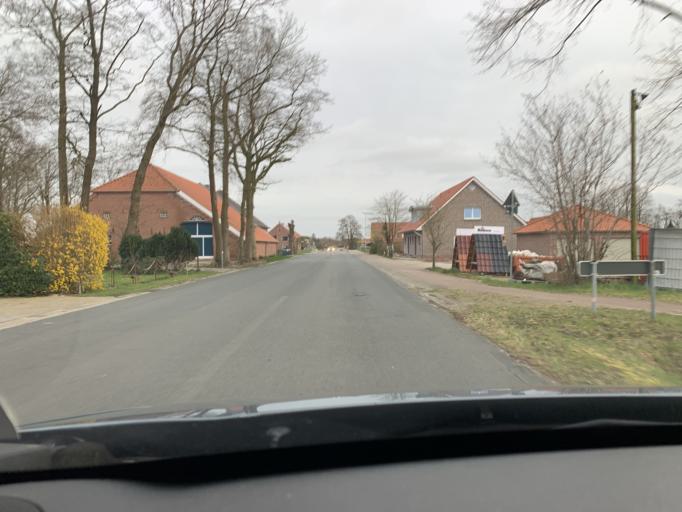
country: DE
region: Lower Saxony
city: Detern
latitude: 53.2427
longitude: 7.7331
